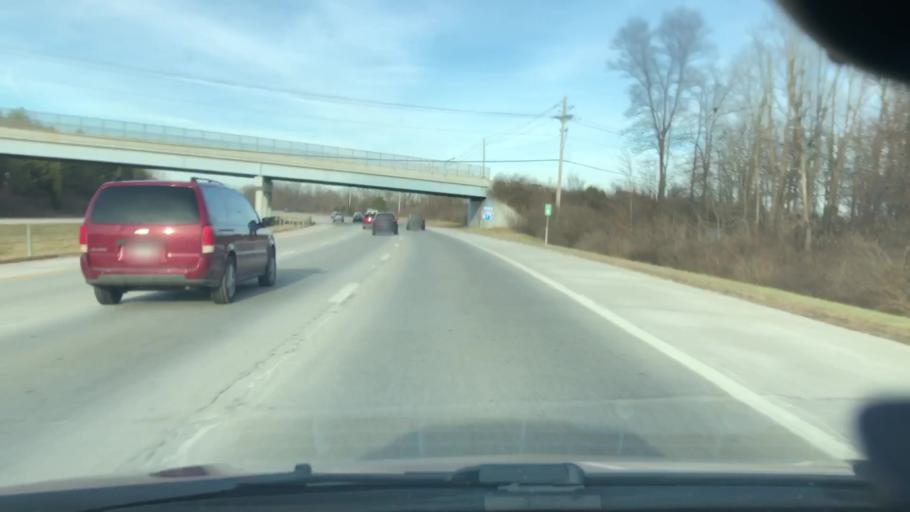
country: US
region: Ohio
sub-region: Greene County
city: Bellbrook
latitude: 39.6593
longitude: -84.1014
